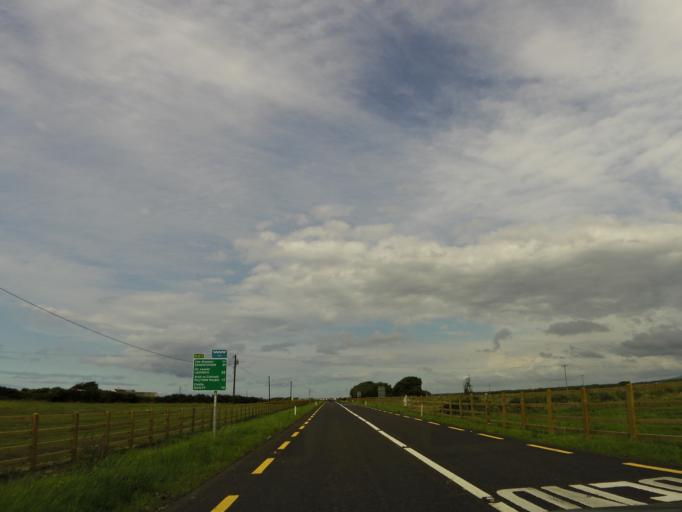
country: IE
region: Munster
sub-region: An Clar
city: Kilrush
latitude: 52.7381
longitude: -9.4823
